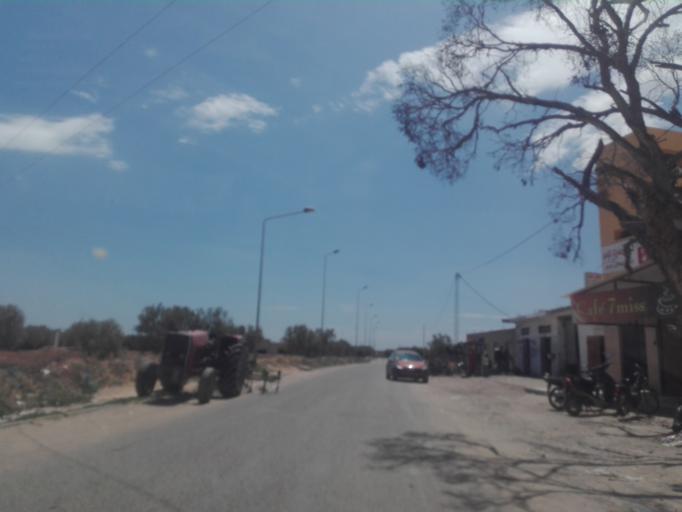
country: TN
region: Safaqis
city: Sfax
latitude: 34.6278
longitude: 10.6003
